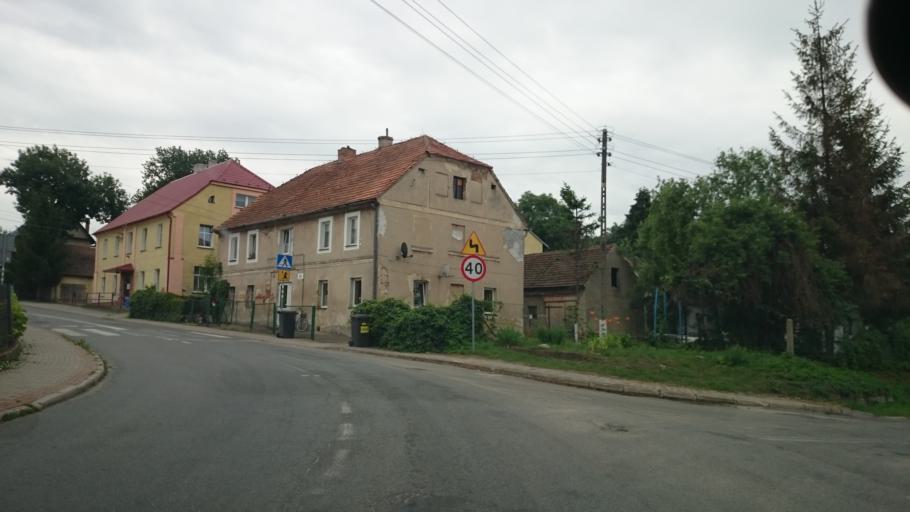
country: PL
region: Lower Silesian Voivodeship
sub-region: Powiat strzelinski
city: Przeworno
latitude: 50.6446
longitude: 17.1727
